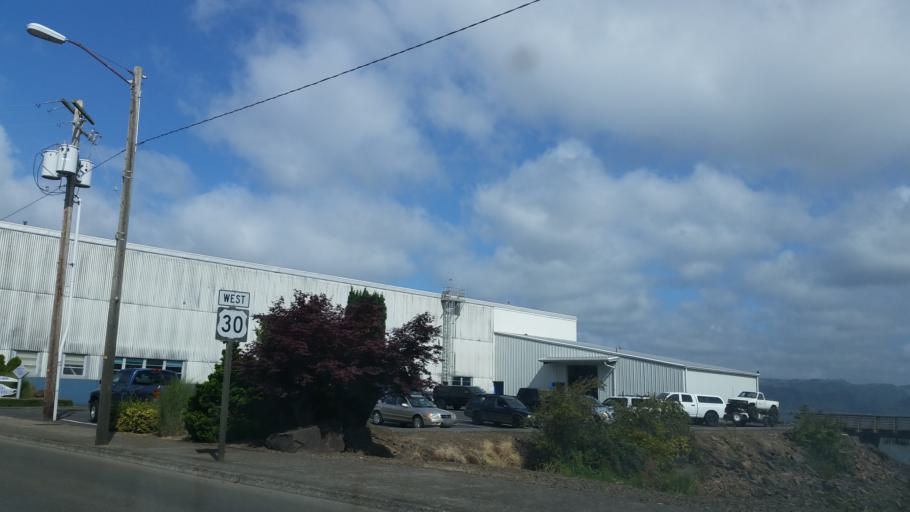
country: US
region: Oregon
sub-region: Clatsop County
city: Astoria
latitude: 46.1907
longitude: -123.8429
